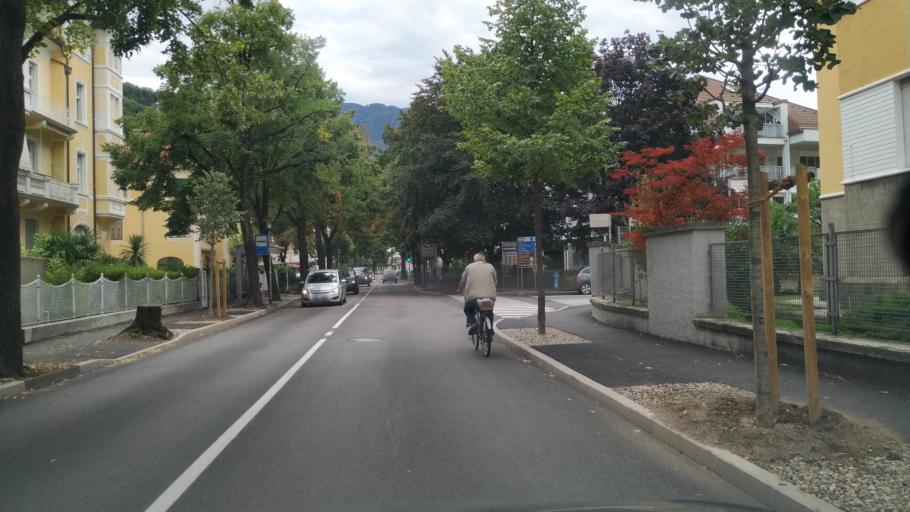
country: IT
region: Trentino-Alto Adige
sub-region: Bolzano
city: Merano
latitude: 46.6752
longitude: 11.1555
